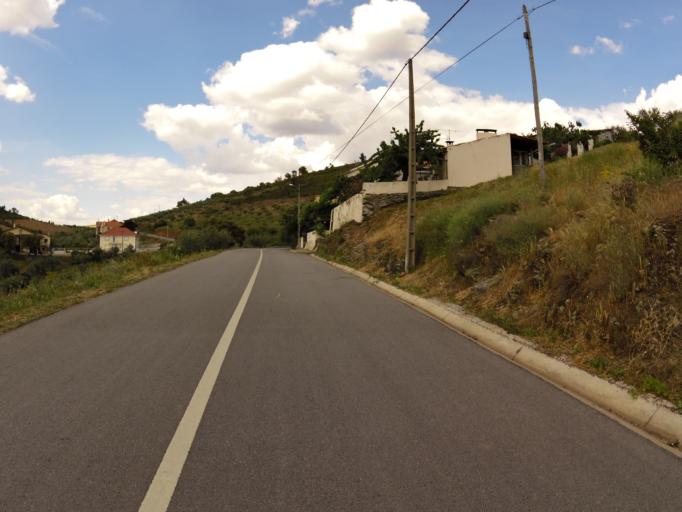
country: PT
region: Braganca
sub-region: Mogadouro
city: Mogadouro
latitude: 41.2442
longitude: -6.7735
